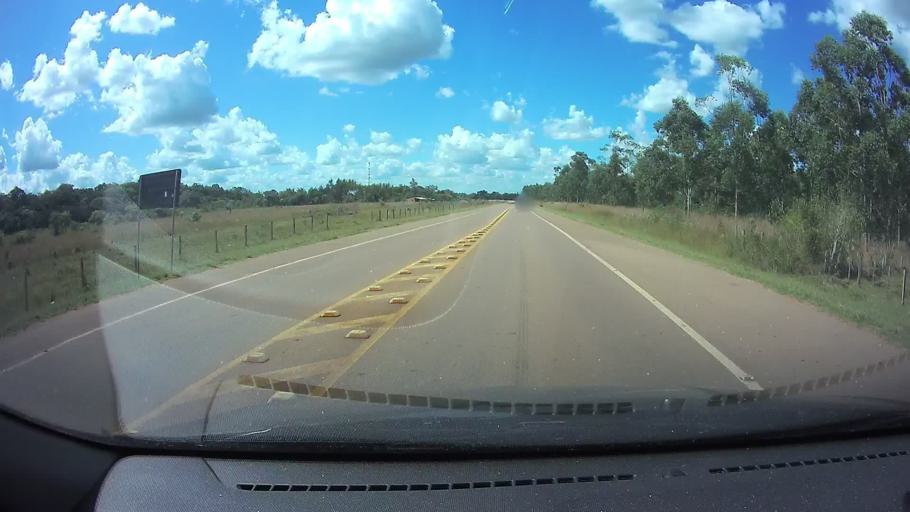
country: PY
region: Guaira
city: Itape
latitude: -25.9081
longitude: -56.6749
